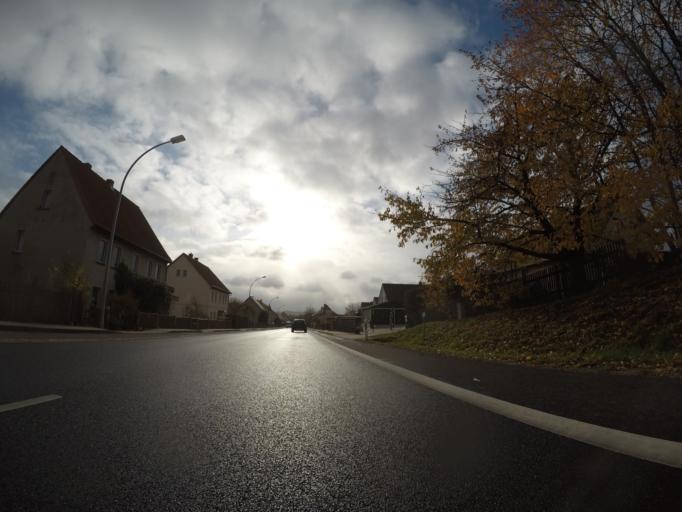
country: DE
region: Thuringia
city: Saara
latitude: 50.9554
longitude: 12.4285
